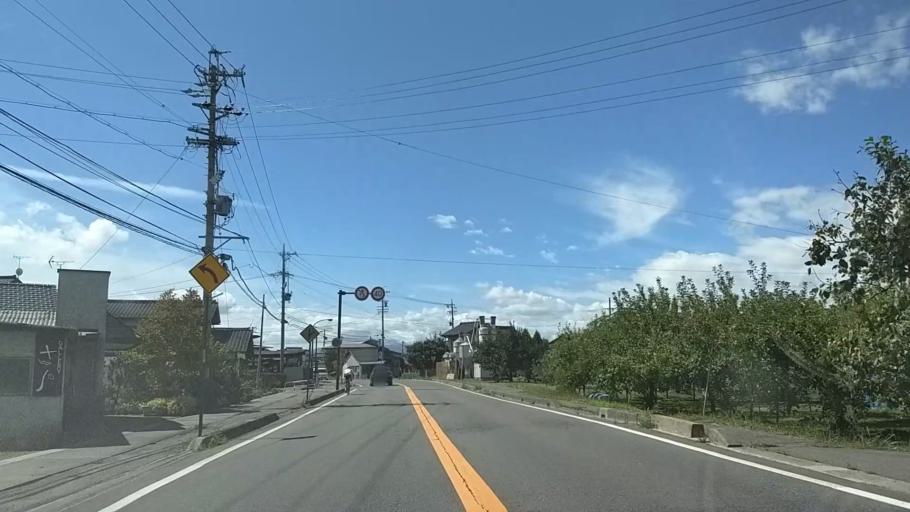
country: JP
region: Nagano
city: Suzaka
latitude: 36.6311
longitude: 138.2645
